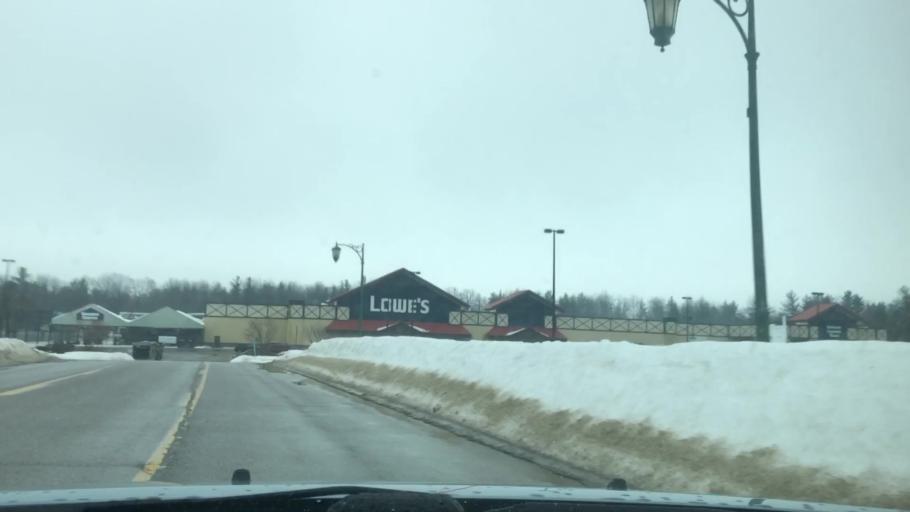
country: US
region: Michigan
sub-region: Otsego County
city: Gaylord
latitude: 45.0244
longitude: -84.6945
